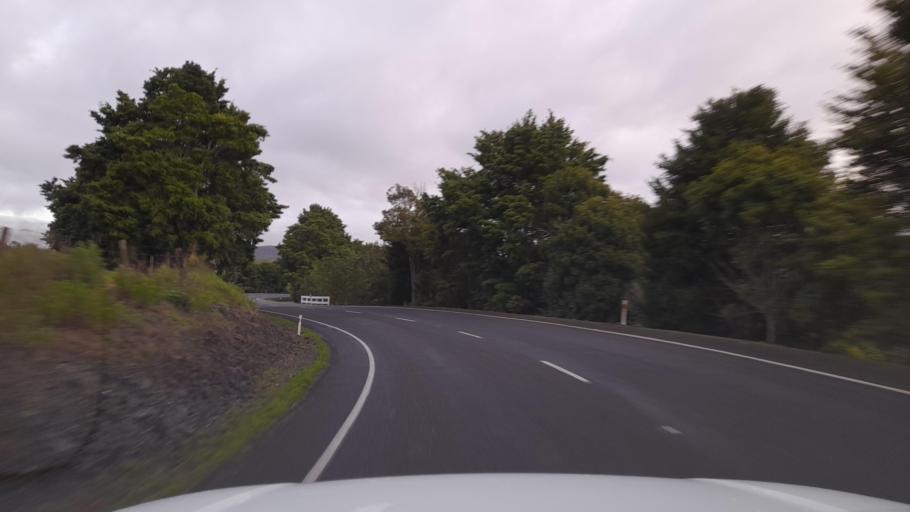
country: NZ
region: Northland
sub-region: Whangarei
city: Maungatapere
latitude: -35.7253
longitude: 174.0431
